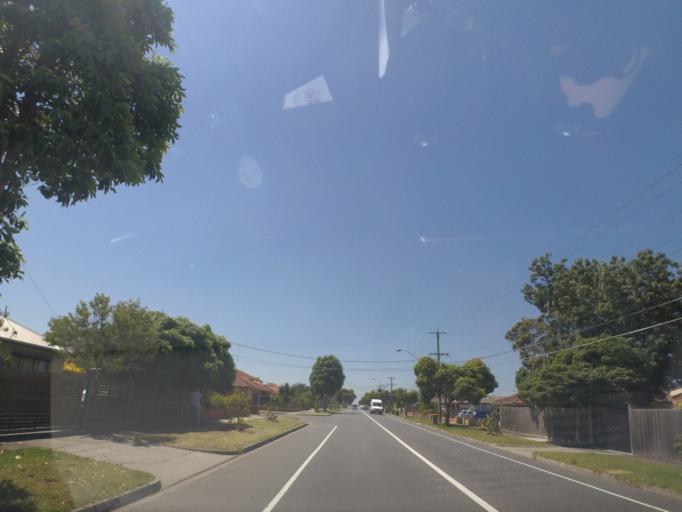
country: AU
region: Victoria
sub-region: Darebin
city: Reservoir
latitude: -37.7133
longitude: 144.9893
